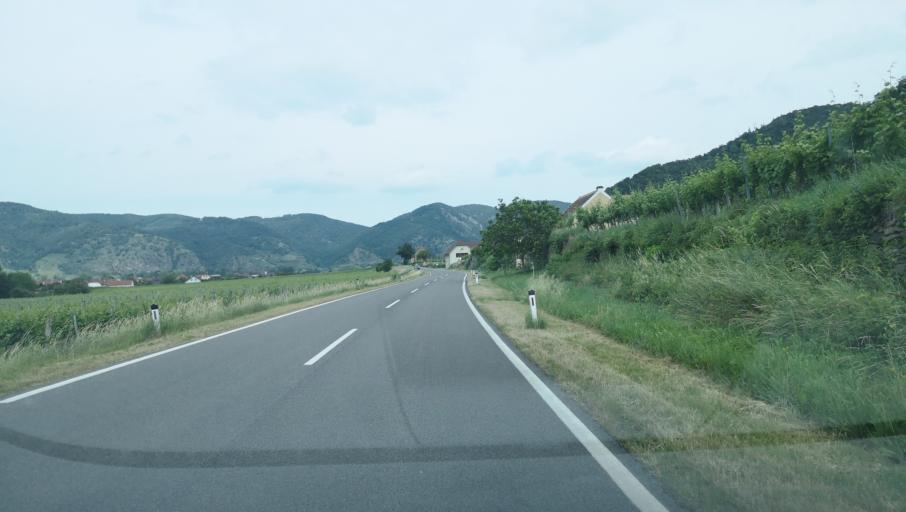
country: AT
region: Lower Austria
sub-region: Politischer Bezirk Krems
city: Durnstein
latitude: 48.3936
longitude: 15.4787
